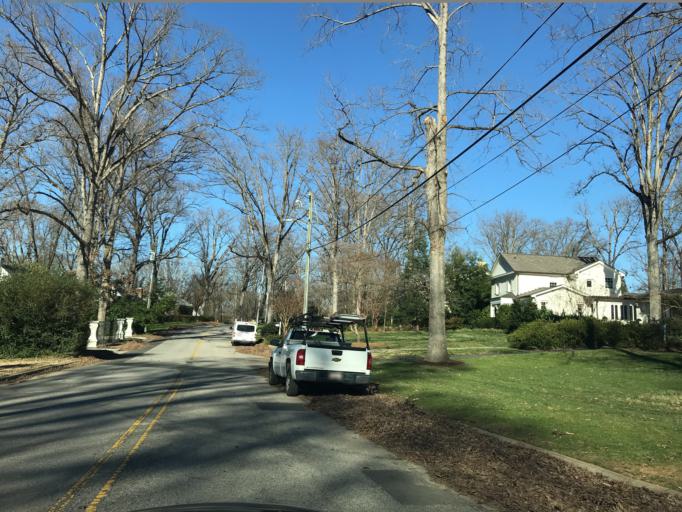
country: US
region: North Carolina
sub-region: Wake County
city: West Raleigh
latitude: 35.8157
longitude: -78.6438
